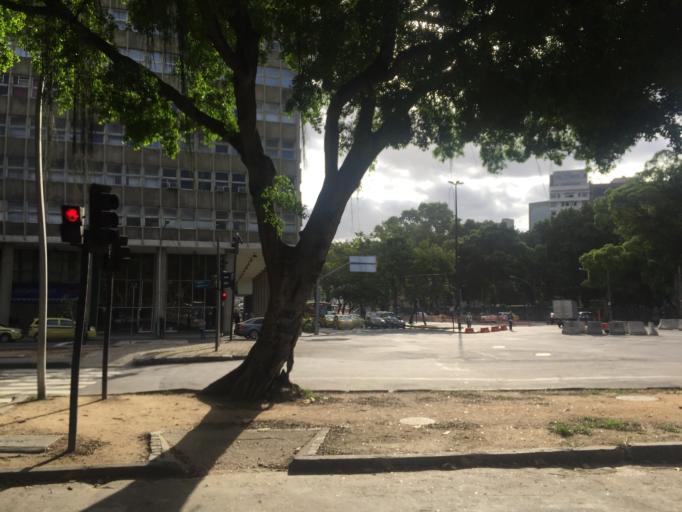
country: BR
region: Rio de Janeiro
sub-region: Rio De Janeiro
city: Rio de Janeiro
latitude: -22.9147
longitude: -43.1759
